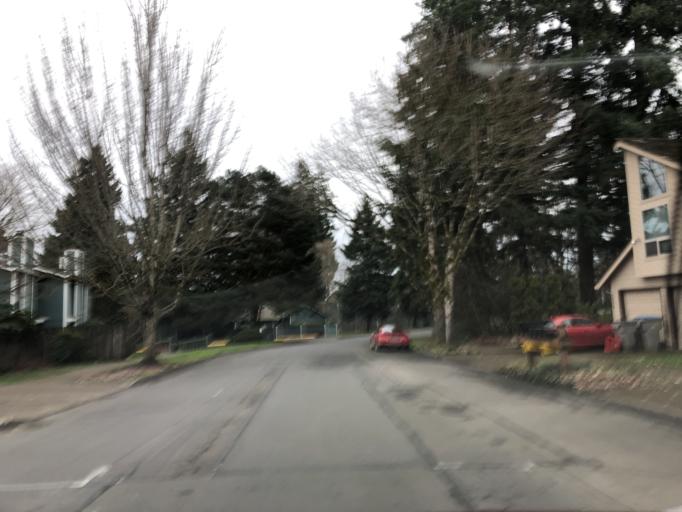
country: US
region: Oregon
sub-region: Washington County
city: Durham
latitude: 45.4172
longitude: -122.7599
